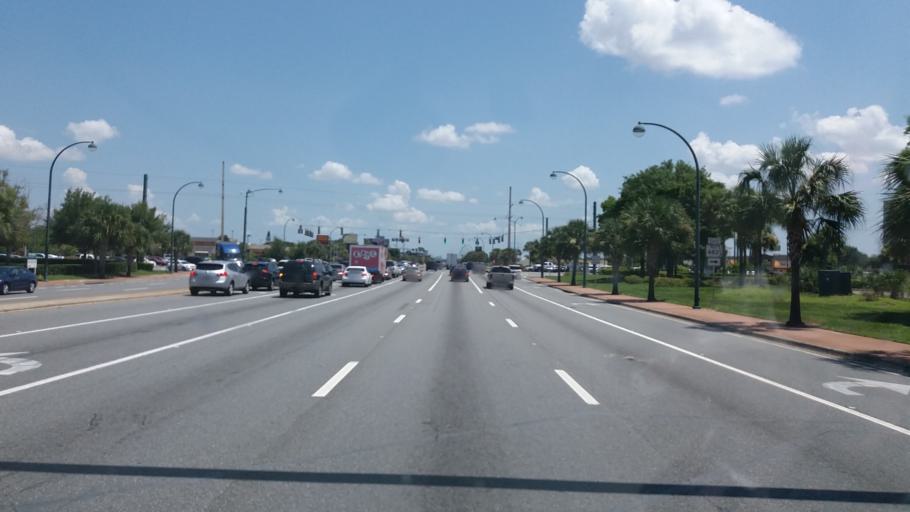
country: US
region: Florida
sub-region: Orange County
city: Sky Lake
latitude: 28.4489
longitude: -81.4011
